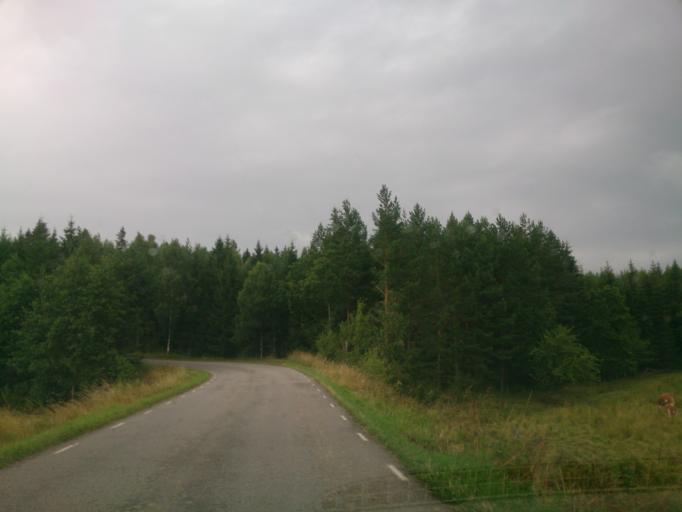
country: SE
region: OEstergoetland
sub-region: Atvidabergs Kommun
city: Atvidaberg
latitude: 58.2847
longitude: 16.0965
